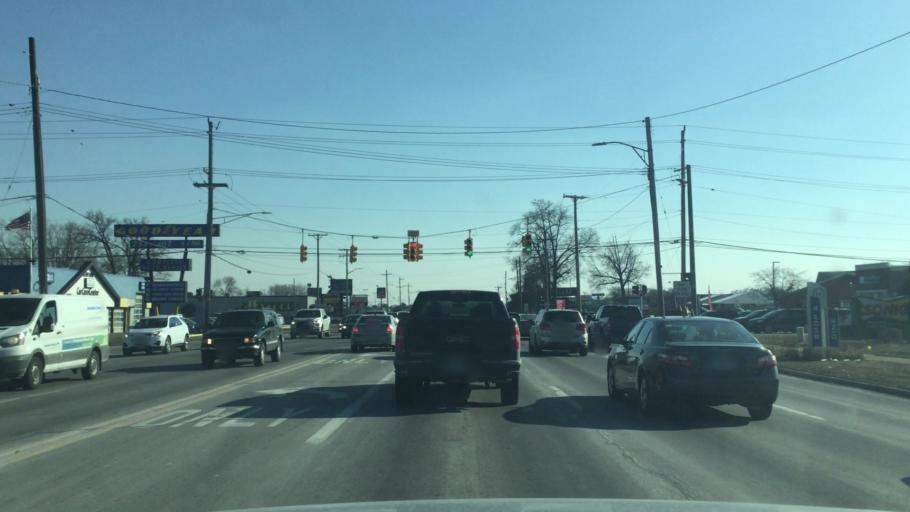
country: US
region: Michigan
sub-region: Wayne County
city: Westland
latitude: 42.3441
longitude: -83.3853
